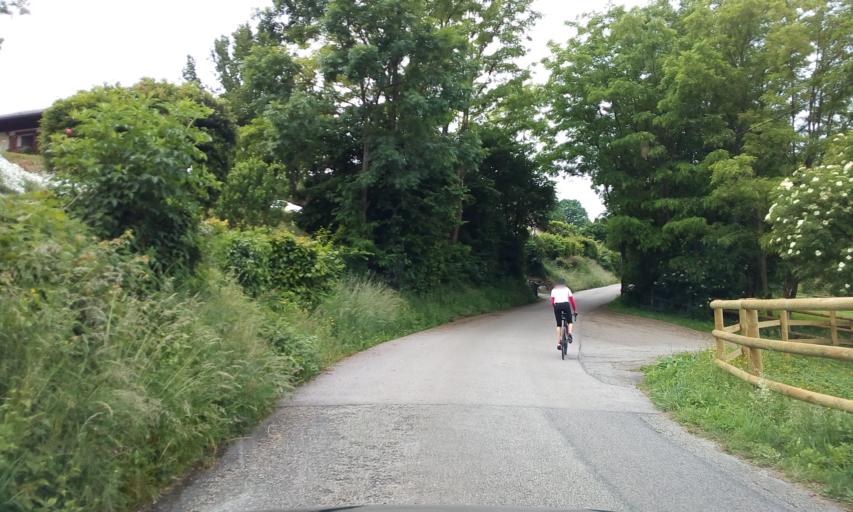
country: FR
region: Rhone-Alpes
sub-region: Departement de la Savoie
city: Barberaz
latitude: 45.5538
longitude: 5.9468
